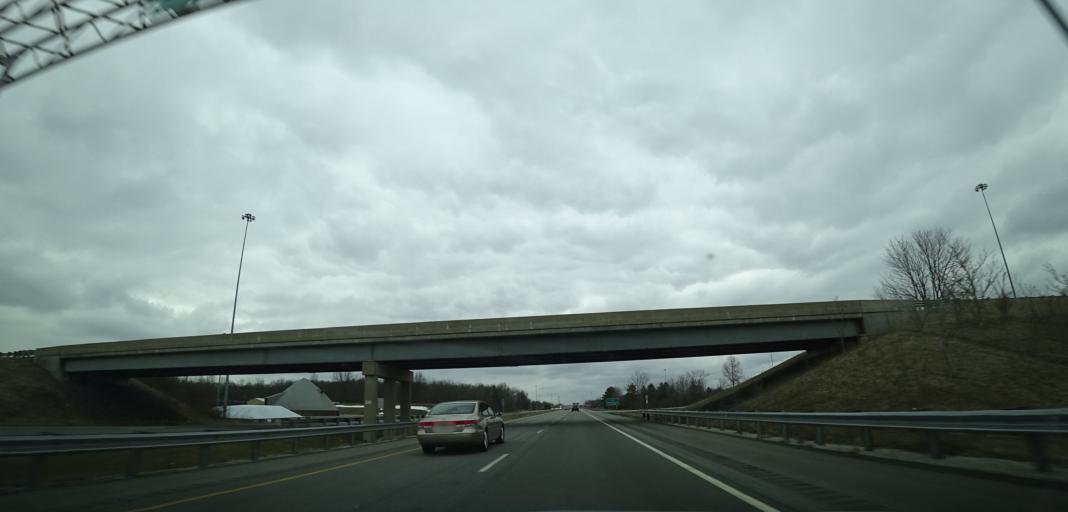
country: US
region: Ohio
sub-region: Trumbull County
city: Lordstown
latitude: 41.1043
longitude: -80.8332
